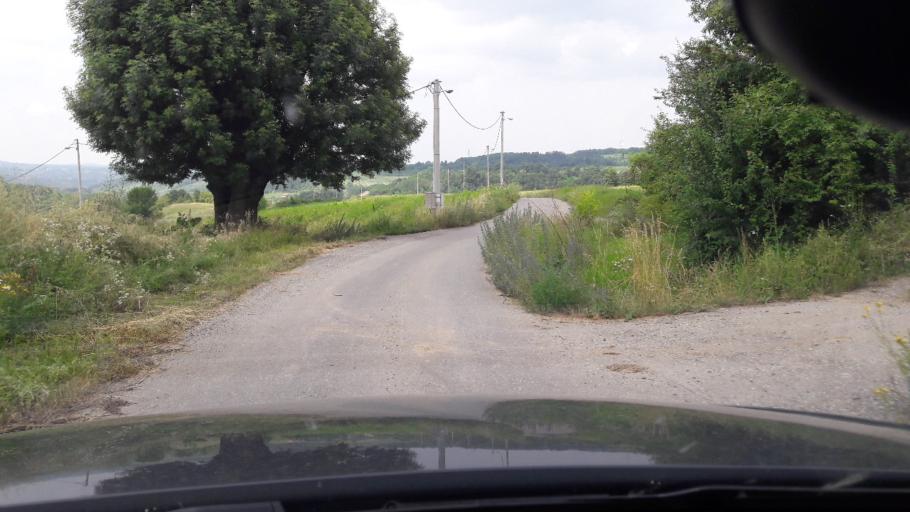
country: RS
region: Central Serbia
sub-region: Belgrade
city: Sopot
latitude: 44.6183
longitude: 20.6027
